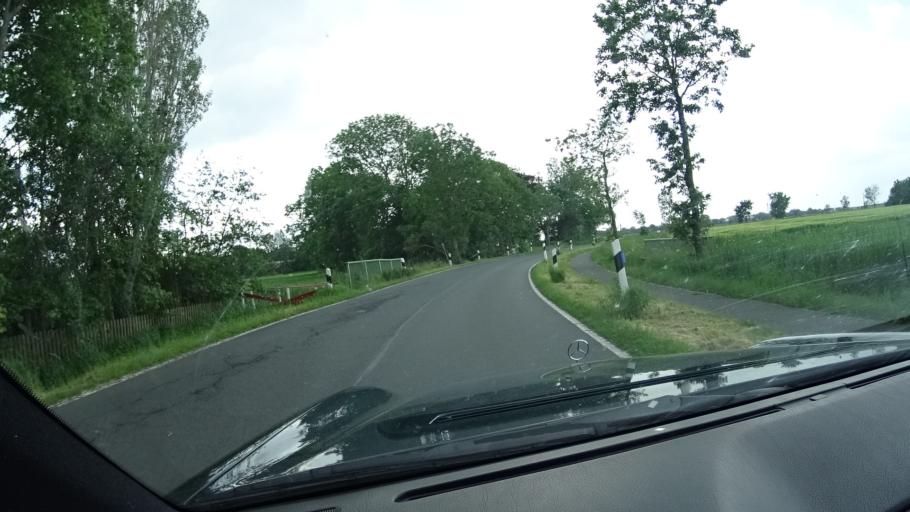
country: DE
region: Lower Saxony
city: Butjadingen
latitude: 53.5816
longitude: 8.2698
